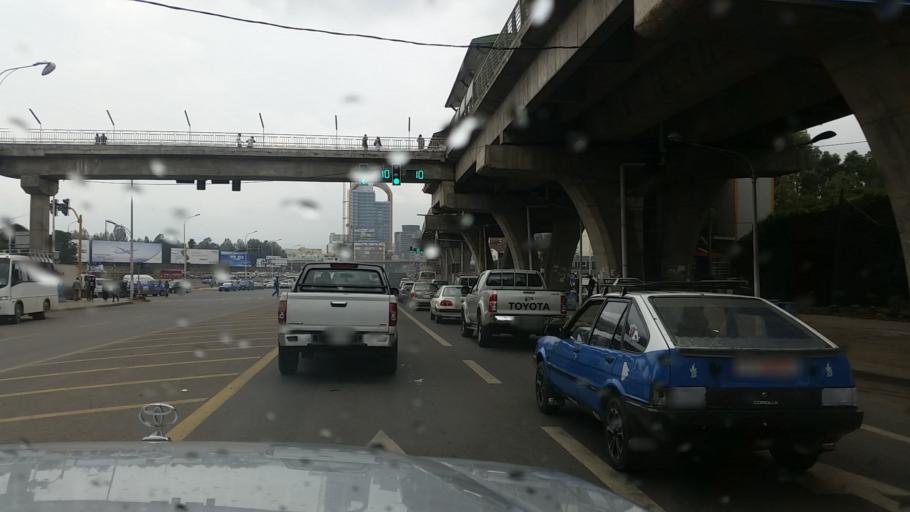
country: ET
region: Adis Abeba
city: Addis Ababa
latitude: 9.0108
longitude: 38.7640
